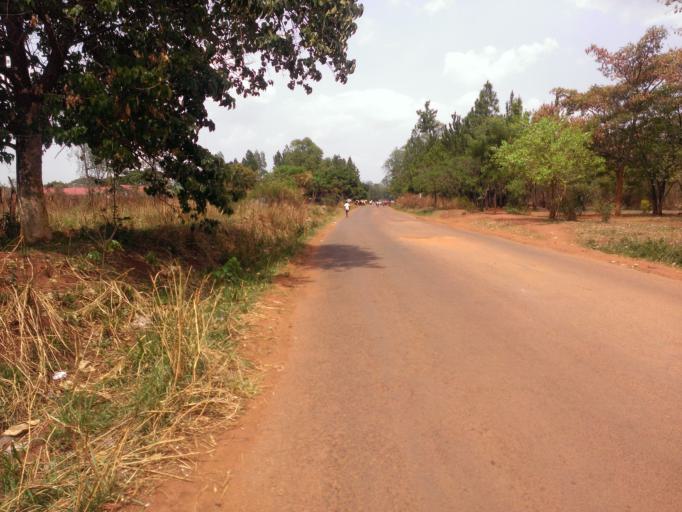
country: UG
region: Northern Region
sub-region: Gulu District
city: Gulu
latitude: 2.7859
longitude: 32.3132
